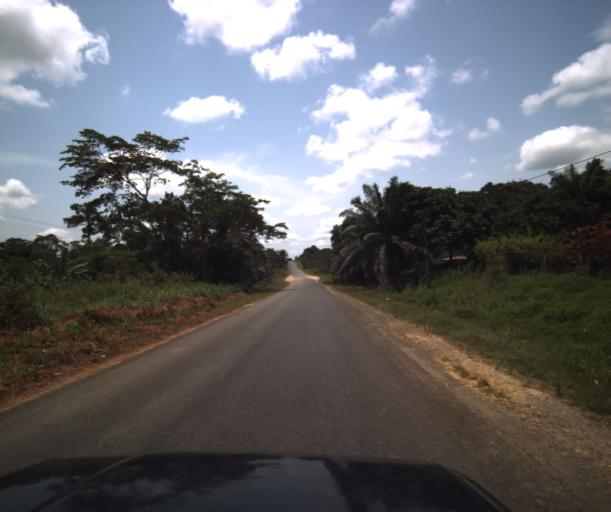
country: CM
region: Centre
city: Eseka
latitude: 3.7159
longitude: 10.7984
